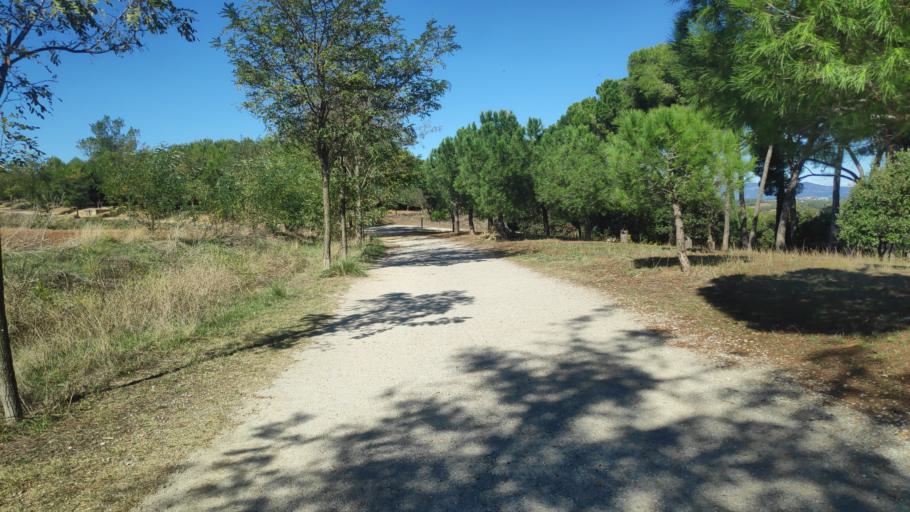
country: ES
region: Catalonia
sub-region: Provincia de Barcelona
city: Mollet del Valles
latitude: 41.5445
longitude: 2.1989
